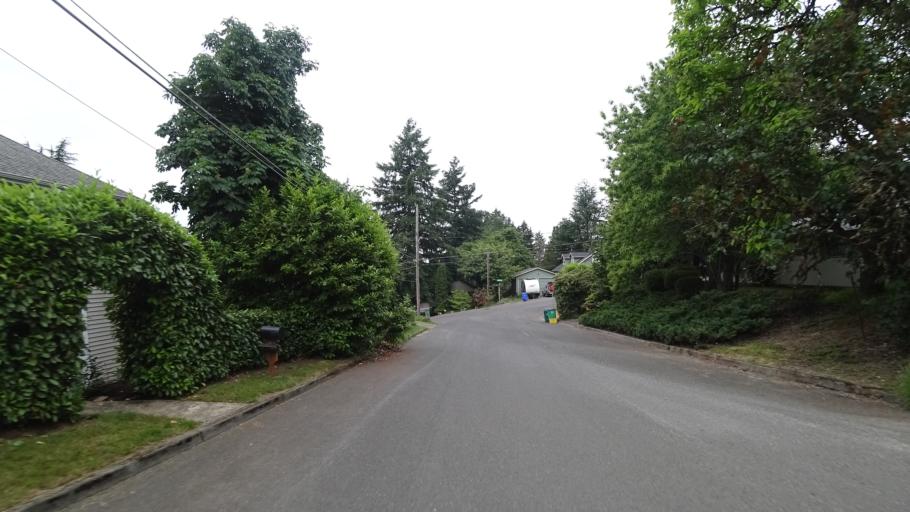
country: US
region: Oregon
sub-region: Clackamas County
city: Lake Oswego
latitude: 45.4555
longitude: -122.6803
